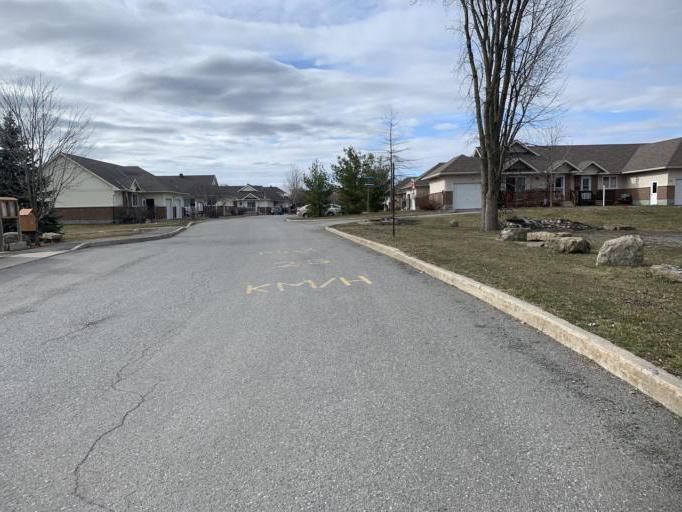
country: CA
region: Ontario
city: Bells Corners
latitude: 45.1940
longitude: -75.8404
